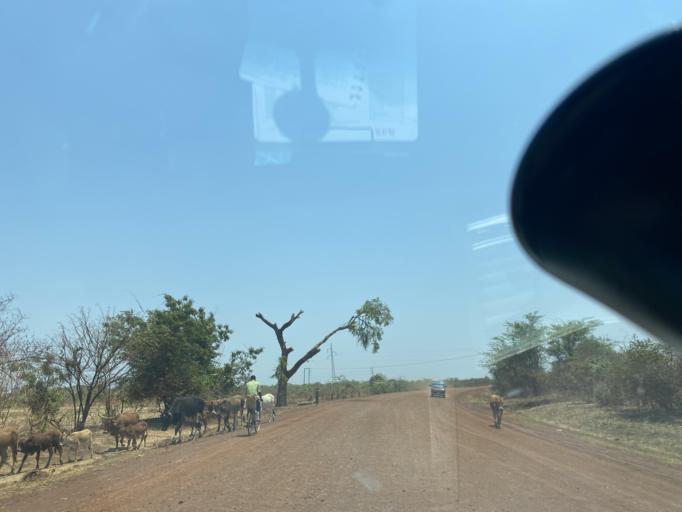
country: ZM
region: Southern
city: Nakambala
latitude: -15.4903
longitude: 27.9013
